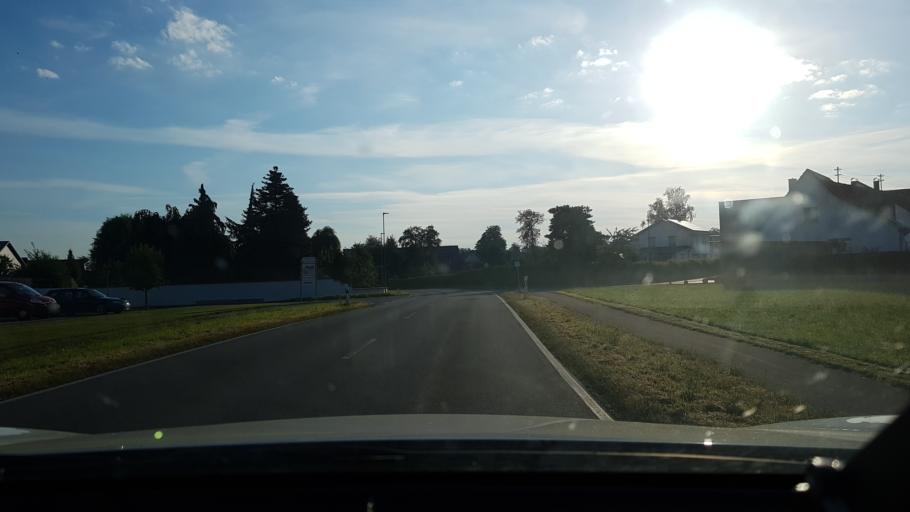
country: DE
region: Baden-Wuerttemberg
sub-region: Tuebingen Region
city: Maselheim
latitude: 48.1559
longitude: 9.8532
